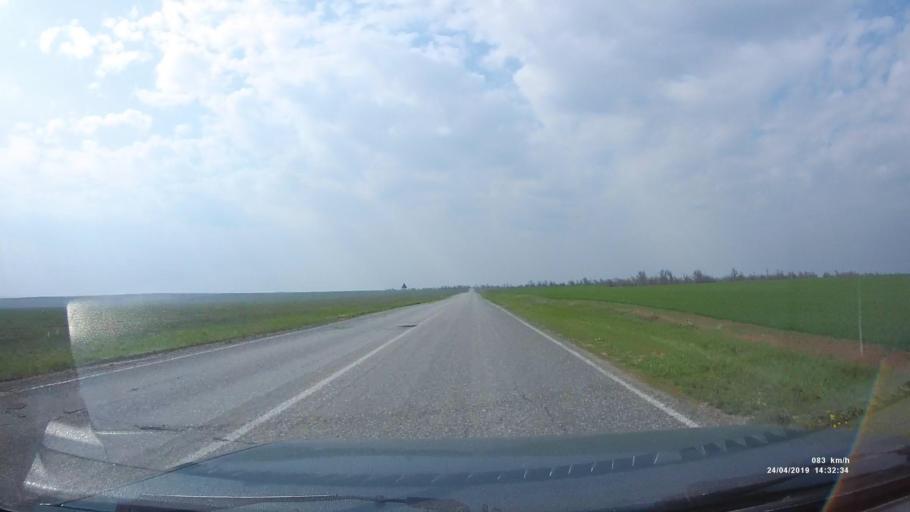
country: RU
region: Kalmykiya
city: Arshan'
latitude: 46.3657
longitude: 43.9670
